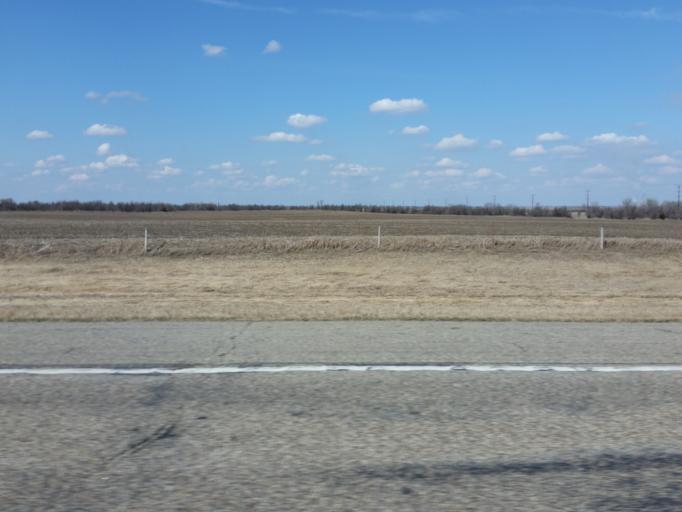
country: US
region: South Dakota
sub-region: Deuel County
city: Clear Lake
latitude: 44.9334
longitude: -96.5136
